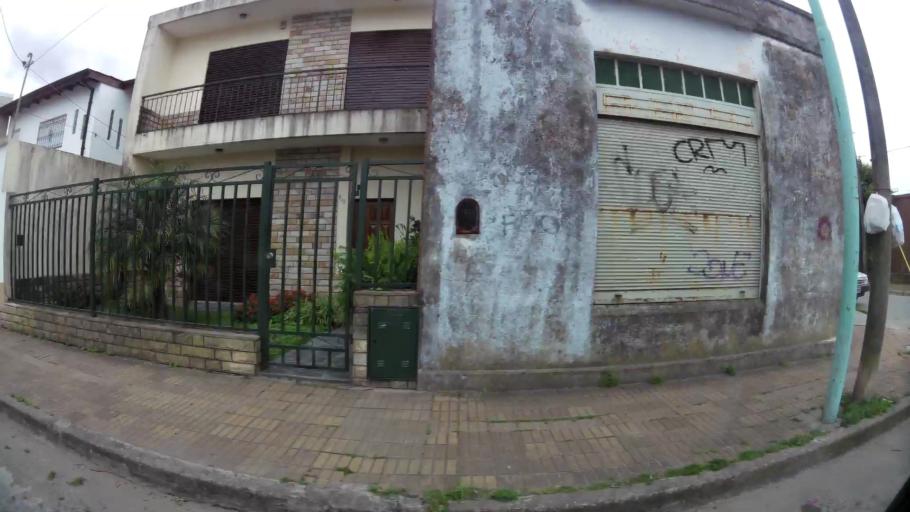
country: AR
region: Buenos Aires
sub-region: Partido de Zarate
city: Zarate
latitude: -34.1082
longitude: -59.0142
